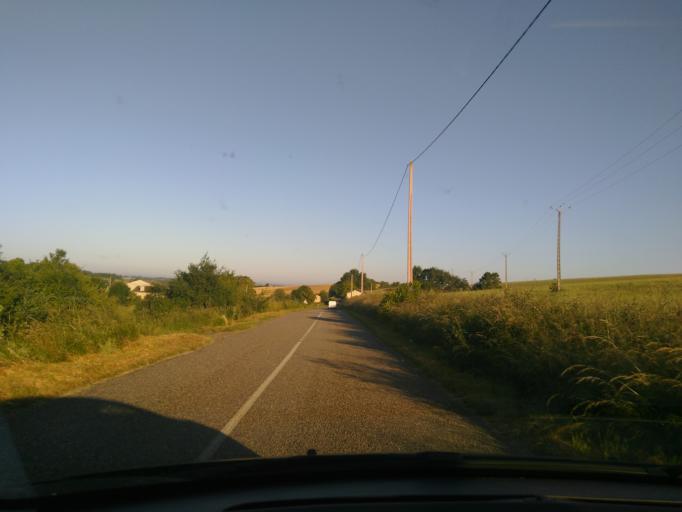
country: FR
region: Midi-Pyrenees
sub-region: Departement du Gers
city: Jegun
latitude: 43.8676
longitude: 0.4937
